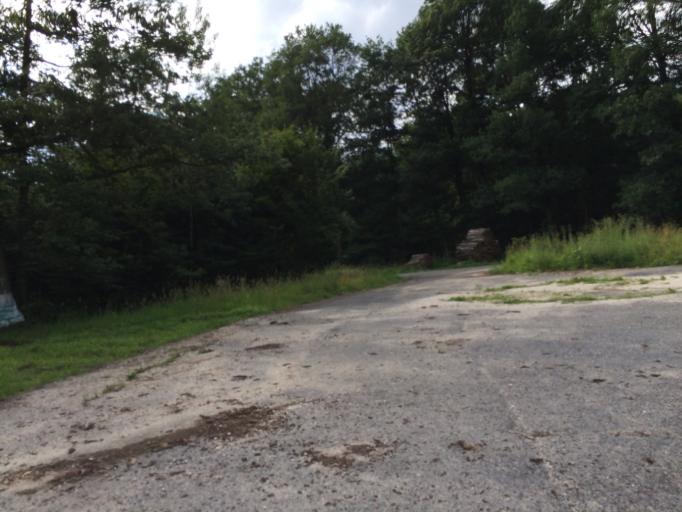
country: FR
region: Ile-de-France
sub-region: Departement de l'Essonne
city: Etiolles
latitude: 48.6576
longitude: 2.4868
